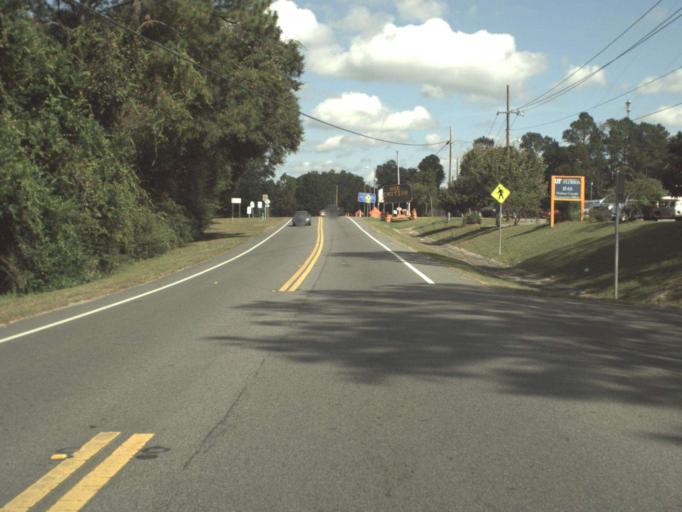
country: US
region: Florida
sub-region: Walton County
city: DeFuniak Springs
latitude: 30.7315
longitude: -86.1144
